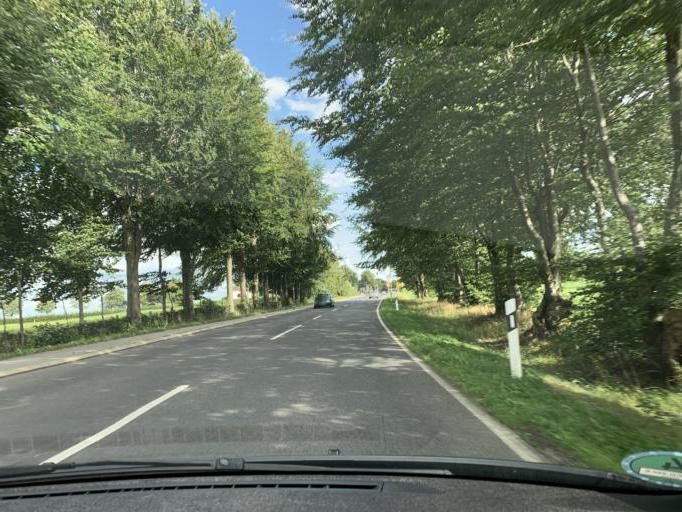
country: DE
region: North Rhine-Westphalia
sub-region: Regierungsbezirk Koln
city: Simmerath
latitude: 50.5942
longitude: 6.2833
